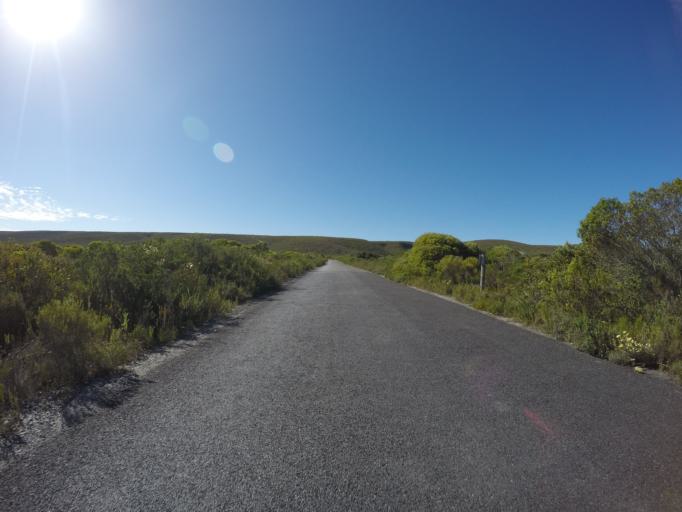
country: ZA
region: Western Cape
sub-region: Overberg District Municipality
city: Bredasdorp
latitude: -34.4319
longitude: 20.4181
